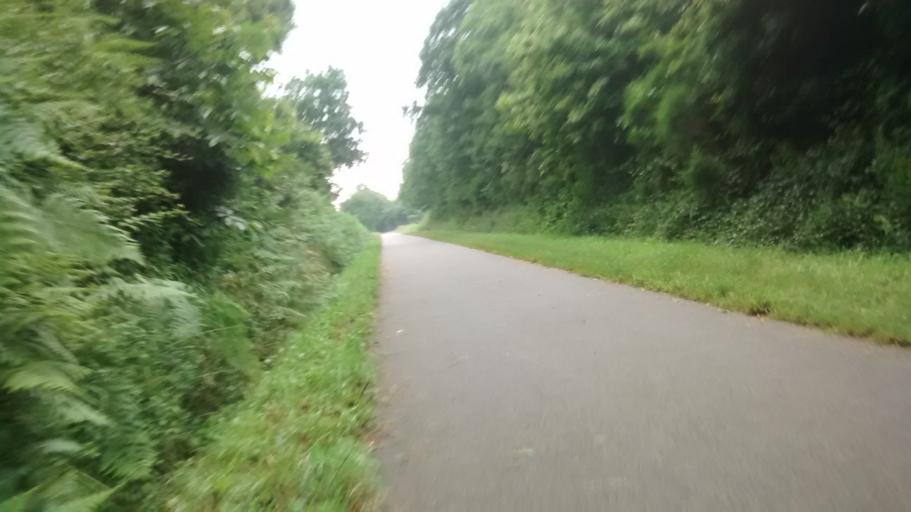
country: FR
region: Brittany
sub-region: Departement du Morbihan
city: Malestroit
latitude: 47.7884
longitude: -2.3987
